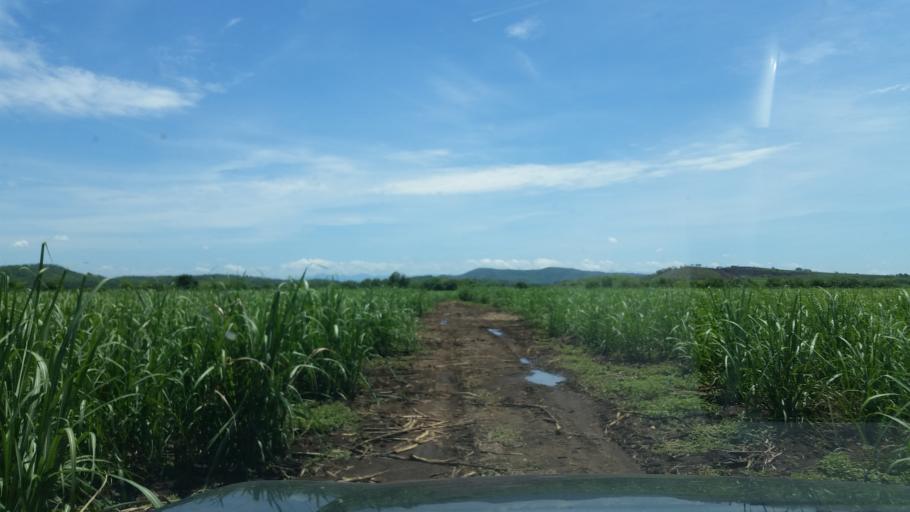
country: NI
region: Chinandega
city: Puerto Morazan
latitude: 12.7700
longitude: -87.1214
